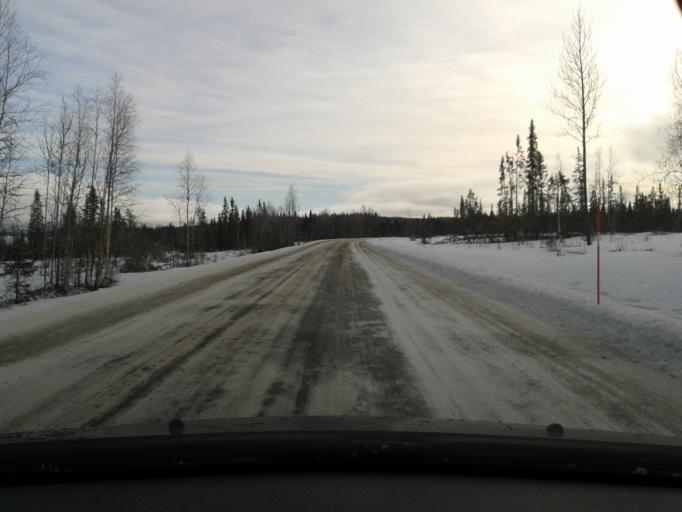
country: SE
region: Vaesterbotten
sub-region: Vilhelmina Kommun
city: Sjoberg
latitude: 64.7507
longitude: 16.1696
